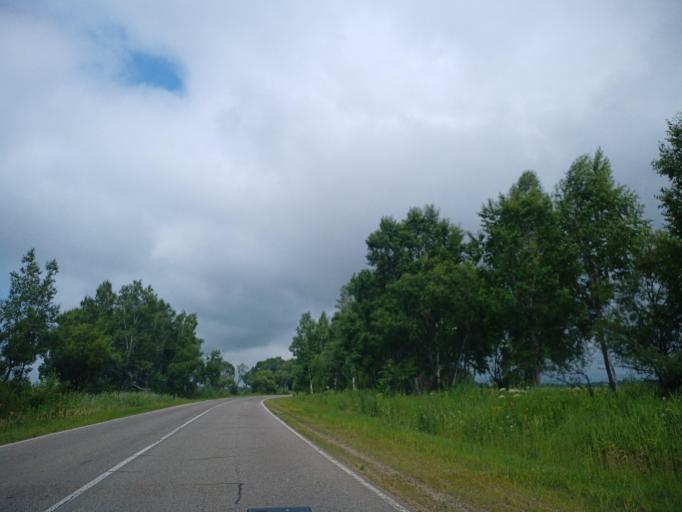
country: RU
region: Primorskiy
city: Novopokrovka
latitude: 45.9733
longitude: 134.1996
